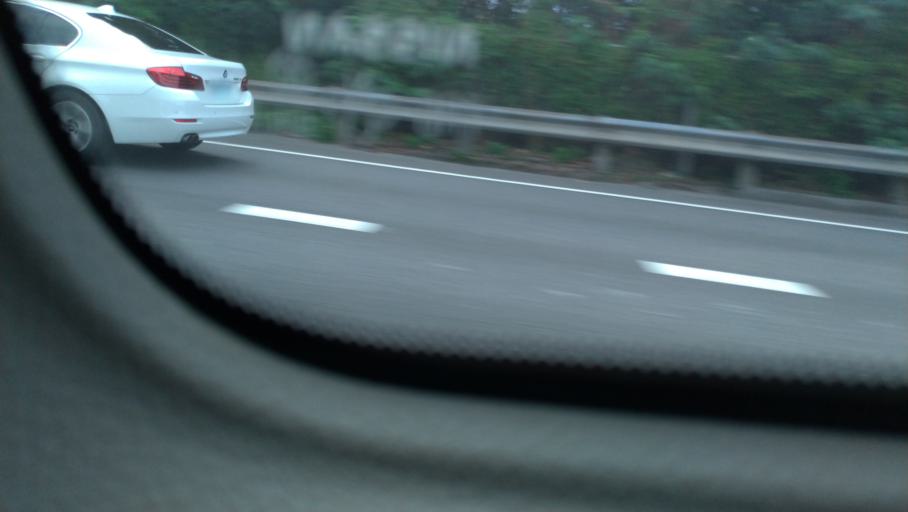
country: TW
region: Taiwan
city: Daxi
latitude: 24.8995
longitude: 121.2689
